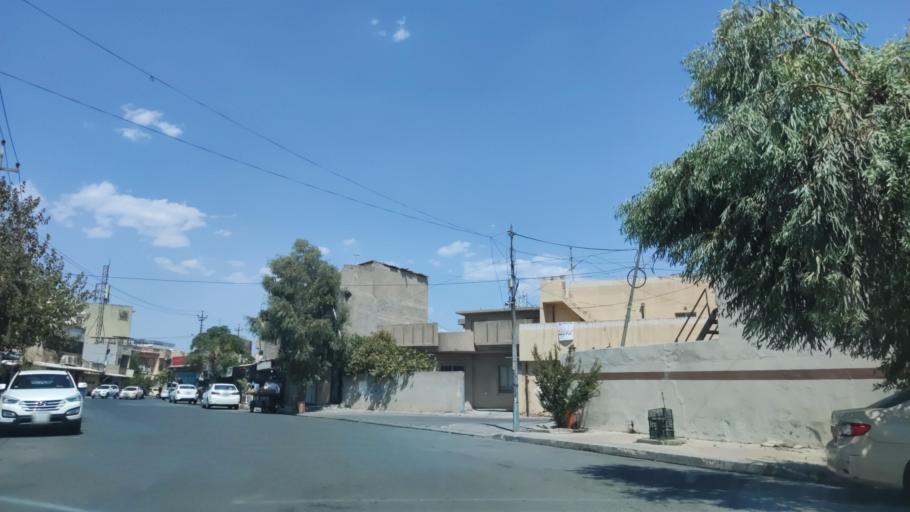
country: IQ
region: Arbil
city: Erbil
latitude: 36.1958
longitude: 44.0215
